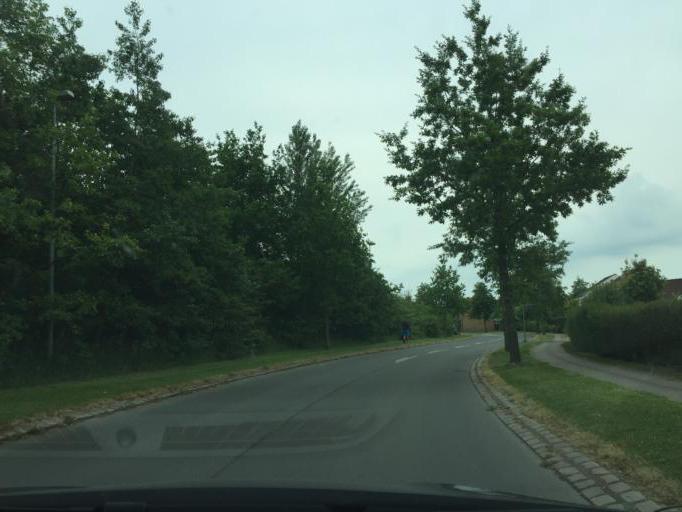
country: DK
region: South Denmark
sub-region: Odense Kommune
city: Neder Holluf
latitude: 55.3631
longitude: 10.4714
